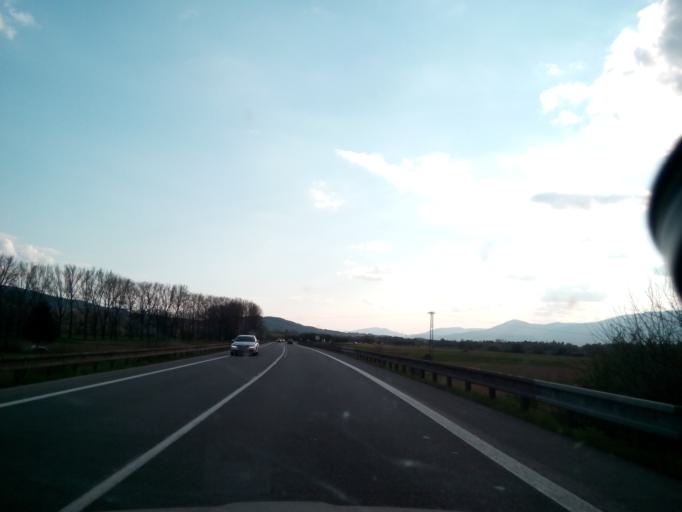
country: SK
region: Zilinsky
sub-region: Okres Zilina
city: Vrutky
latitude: 49.1167
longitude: 19.0267
